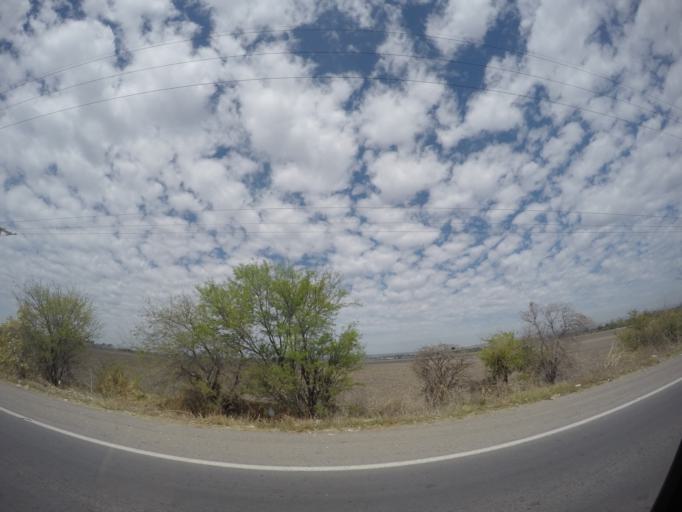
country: MX
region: Guanajuato
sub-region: Leon
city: San Antonio de los Tepetates
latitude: 21.0418
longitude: -101.6921
